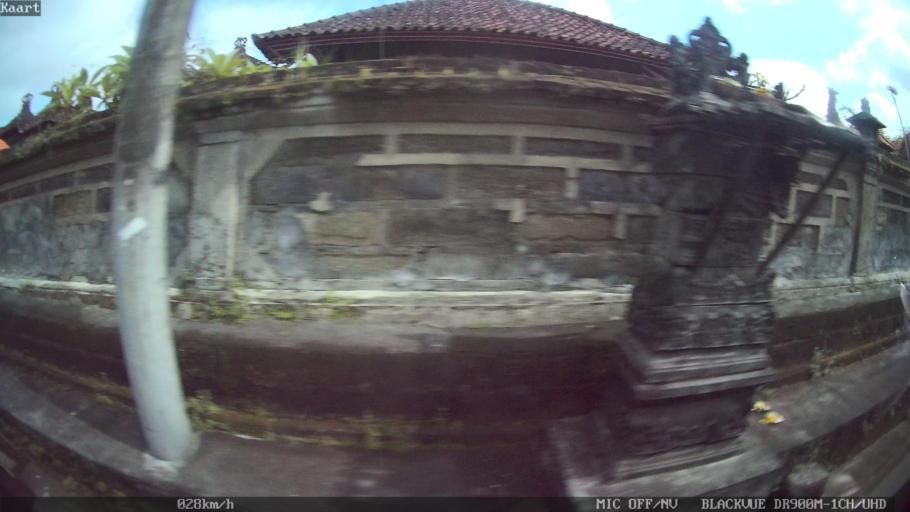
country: ID
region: Bali
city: Banjar Pesalakan
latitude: -8.5210
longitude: 115.3093
